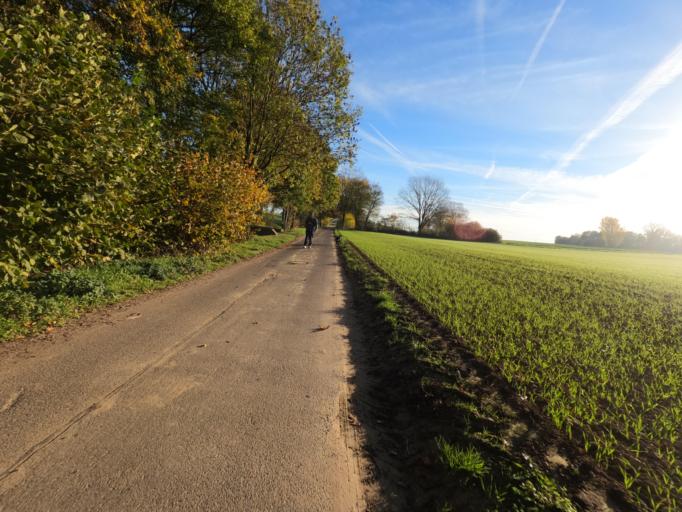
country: DE
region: North Rhine-Westphalia
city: Erkelenz
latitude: 51.0310
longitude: 6.3426
